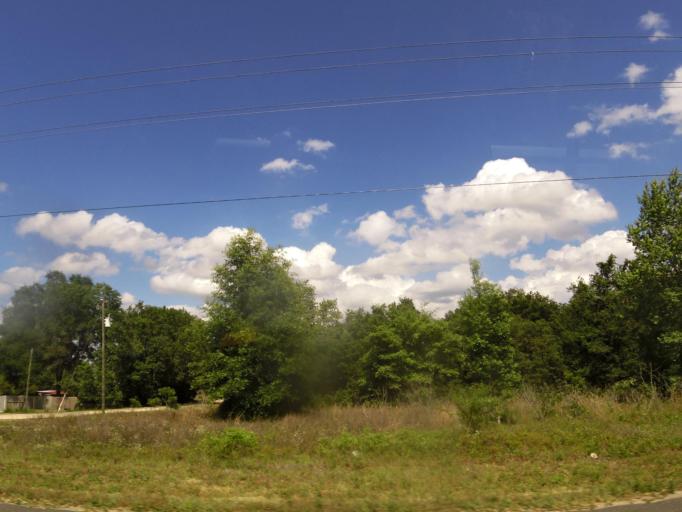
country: US
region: Florida
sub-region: Clay County
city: Keystone Heights
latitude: 29.8288
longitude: -81.9225
